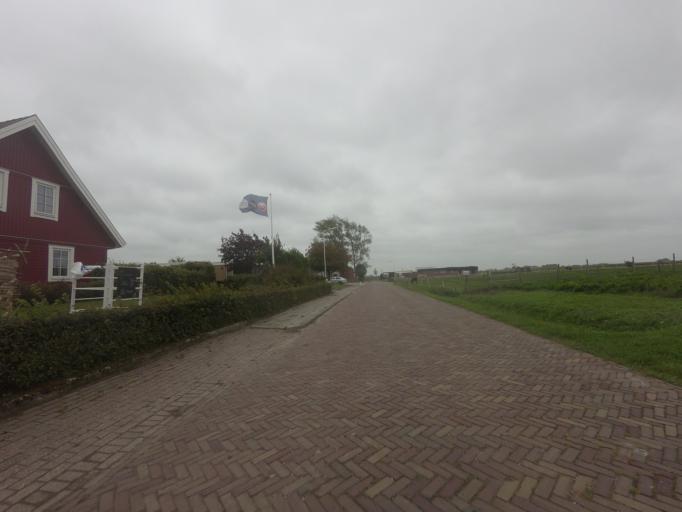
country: NL
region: Friesland
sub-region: Gemeente Ferwerderadiel
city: Ferwert
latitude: 53.3497
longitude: 5.8612
